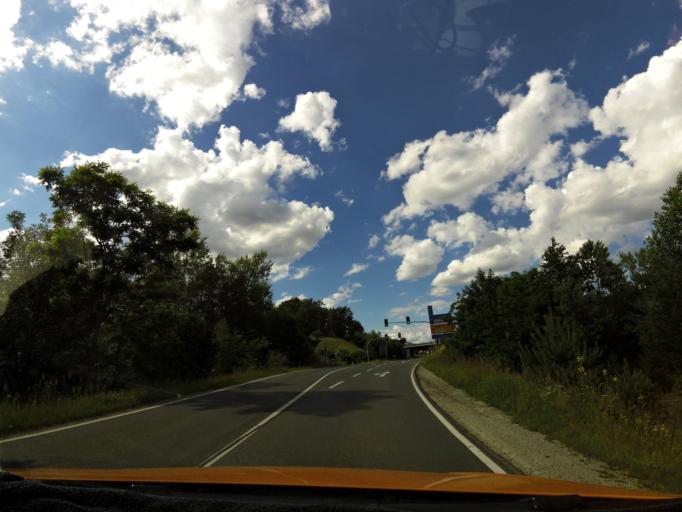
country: DE
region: Brandenburg
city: Wildau
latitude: 52.3109
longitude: 13.6639
